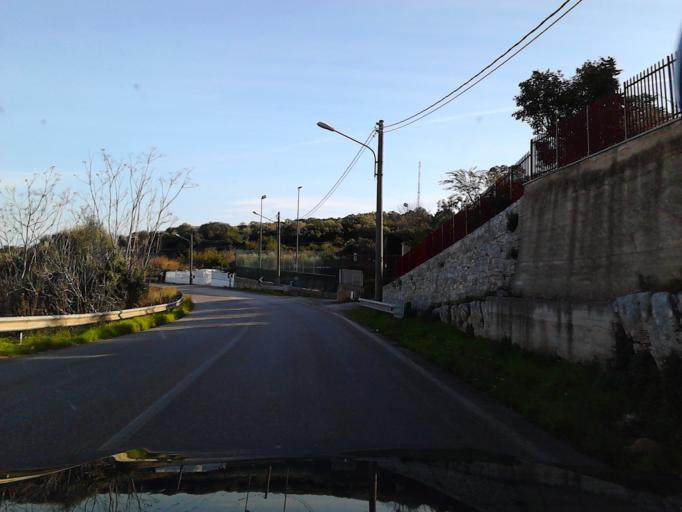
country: IT
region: Apulia
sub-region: Provincia di Bari
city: Mola di Bari
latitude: 41.0390
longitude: 17.0516
